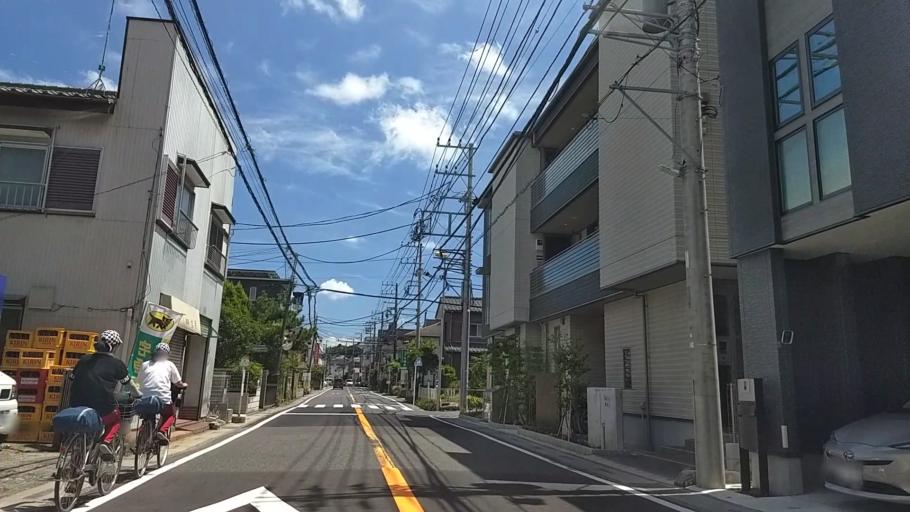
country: JP
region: Kanagawa
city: Kamakura
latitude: 35.3446
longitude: 139.5335
